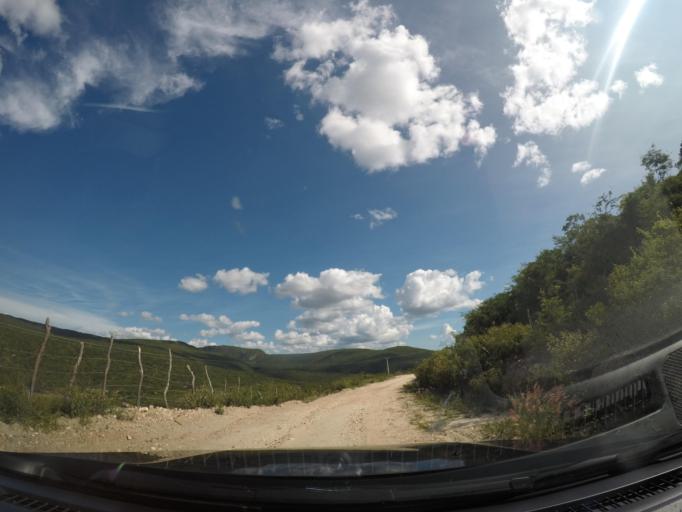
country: BR
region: Bahia
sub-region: Barra Da Estiva
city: Barra da Estiva
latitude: -13.2103
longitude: -41.5911
